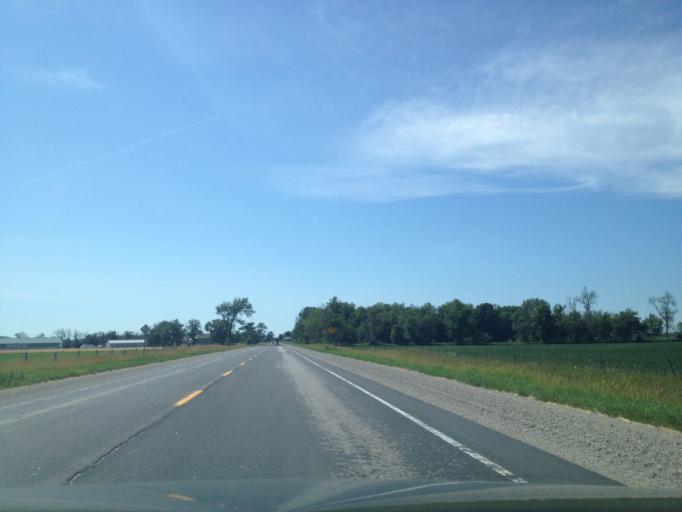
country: CA
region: Ontario
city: Stratford
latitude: 43.4968
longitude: -80.8660
